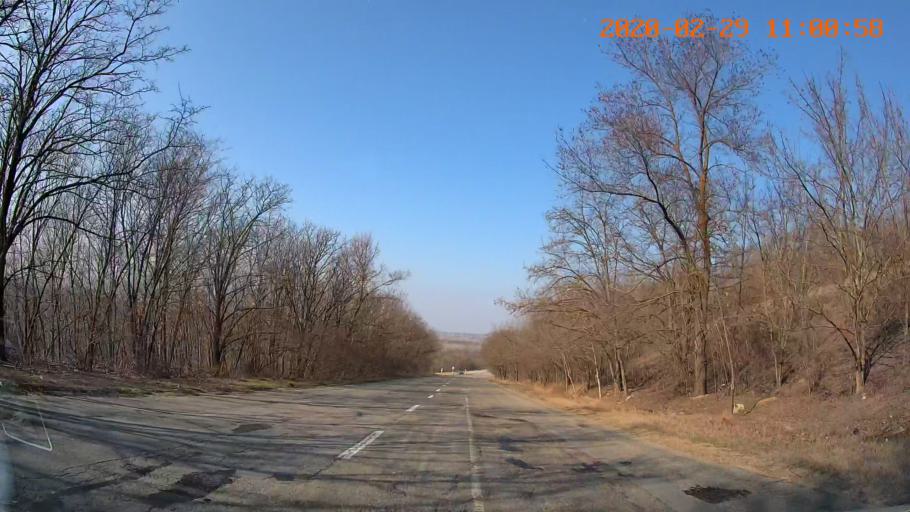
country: MD
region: Telenesti
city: Grigoriopol
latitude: 47.1612
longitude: 29.2670
